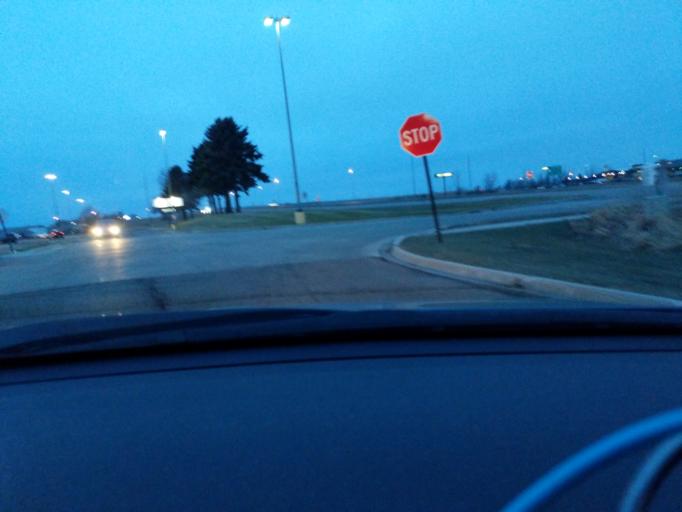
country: US
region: Minnesota
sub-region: Kandiyohi County
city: Willmar
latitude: 45.0947
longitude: -95.0419
